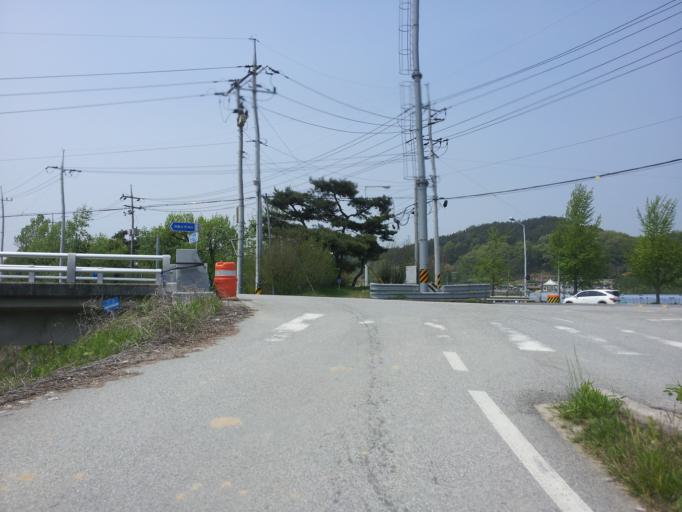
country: KR
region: Daejeon
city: Daejeon
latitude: 36.2669
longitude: 127.2796
